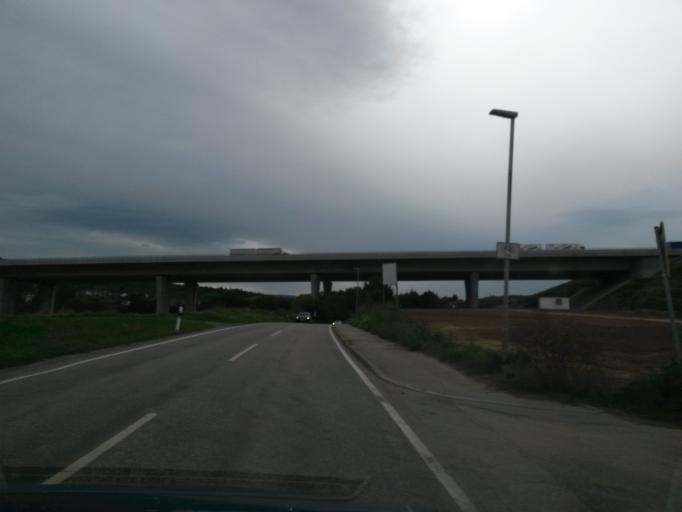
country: DE
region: Baden-Wuerttemberg
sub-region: Karlsruhe Region
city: Konigsbach-Stein
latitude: 48.9355
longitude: 8.5715
